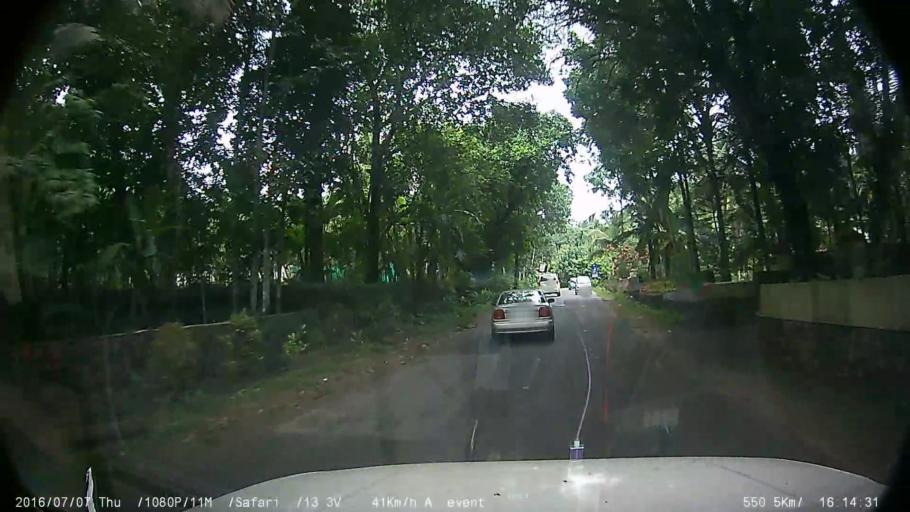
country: IN
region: Kerala
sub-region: Kottayam
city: Palackattumala
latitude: 9.7683
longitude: 76.6103
